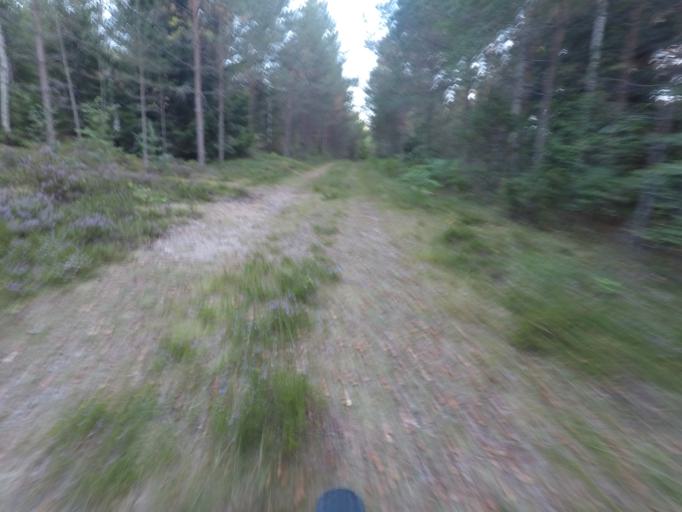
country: SE
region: Soedermanland
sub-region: Eskilstuna Kommun
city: Kvicksund
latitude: 59.4172
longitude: 16.3156
